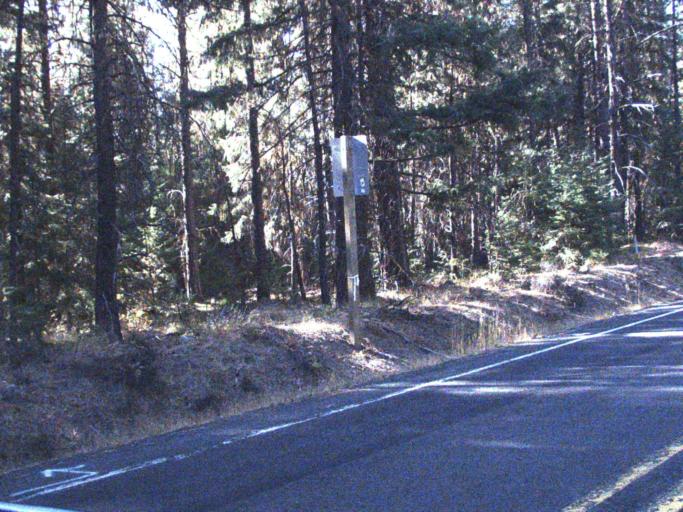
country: US
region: Washington
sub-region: Yakima County
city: Tieton
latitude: 46.6722
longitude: -121.0860
